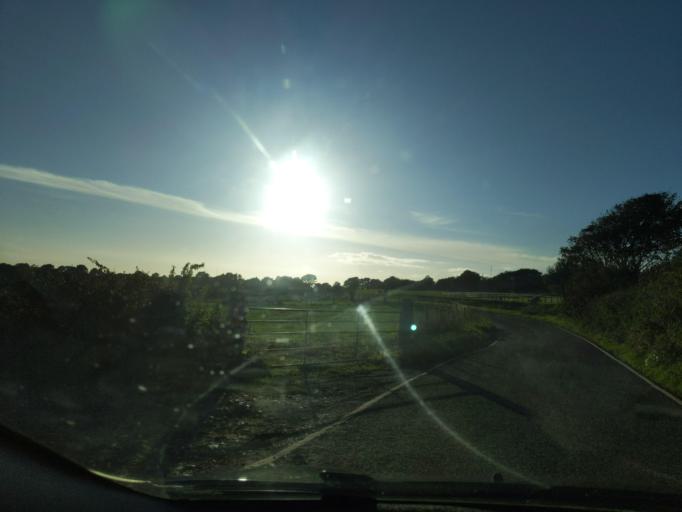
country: GB
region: England
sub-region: Plymouth
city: Plymstock
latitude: 50.3450
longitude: -4.1099
